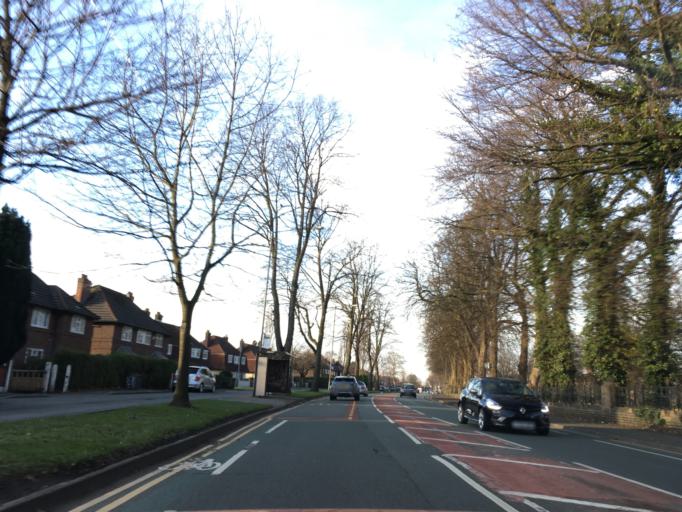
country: GB
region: England
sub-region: Manchester
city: Chorlton cum Hardy
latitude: 53.4286
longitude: -2.2635
